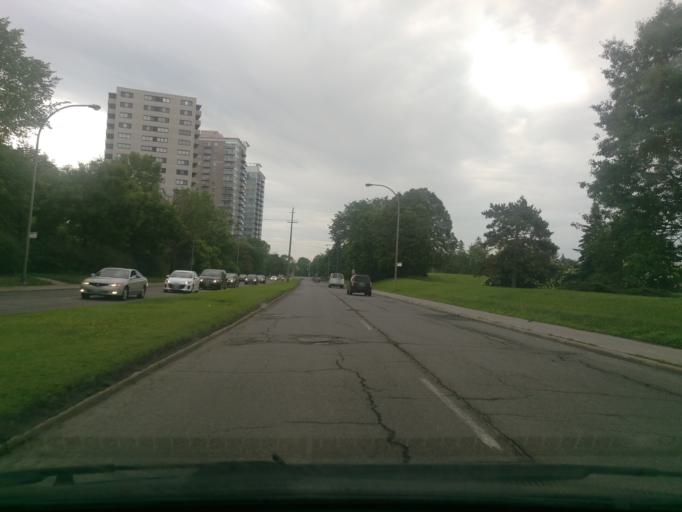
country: CA
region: Ontario
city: Ottawa
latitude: 45.4378
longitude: -75.6760
